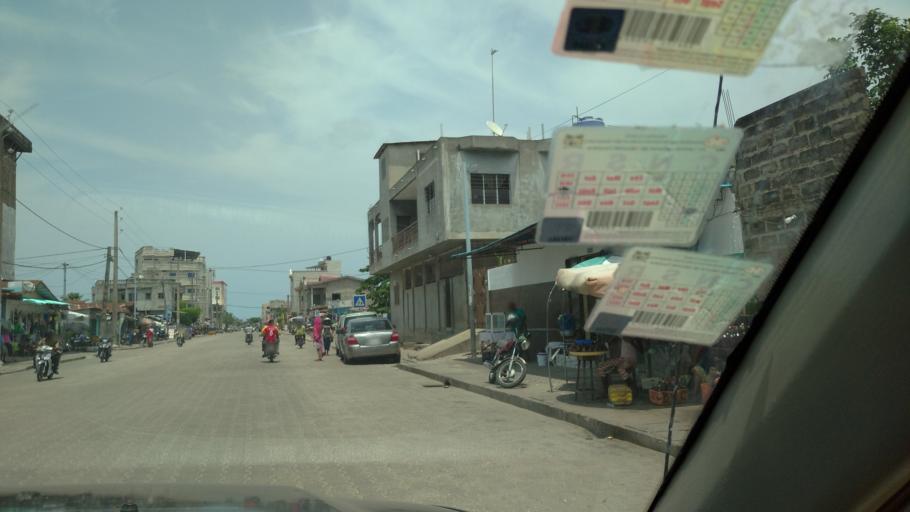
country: BJ
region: Littoral
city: Cotonou
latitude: 6.3918
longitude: 2.4541
